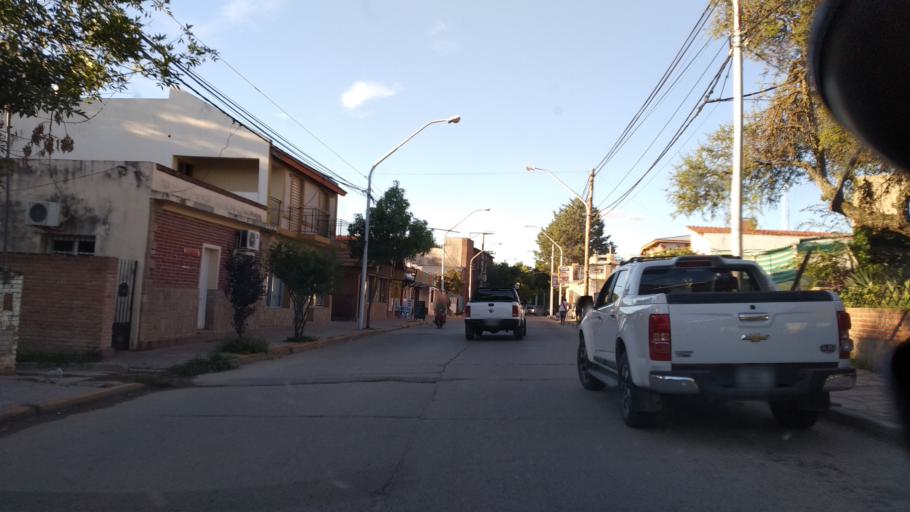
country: AR
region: Cordoba
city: Mina Clavero
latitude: -31.7169
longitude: -65.0059
